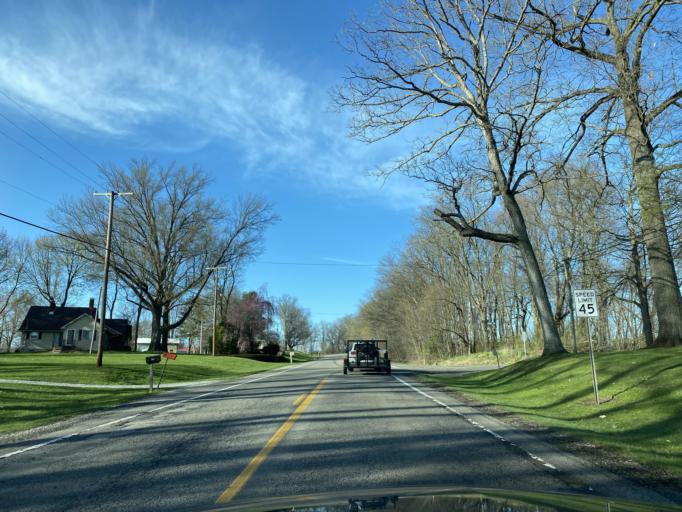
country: US
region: Ohio
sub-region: Wayne County
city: Wooster
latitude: 40.7624
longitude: -81.9740
